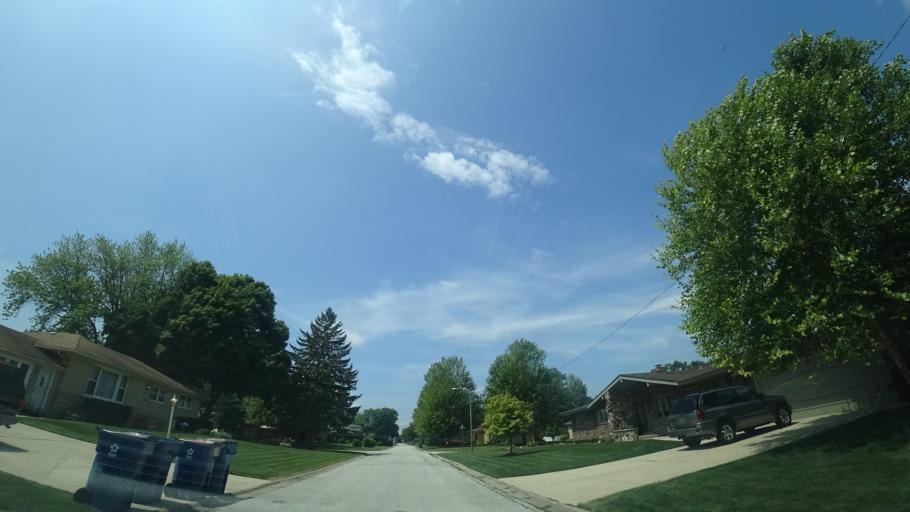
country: US
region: Illinois
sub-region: Cook County
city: Crestwood
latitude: 41.6641
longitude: -87.7701
